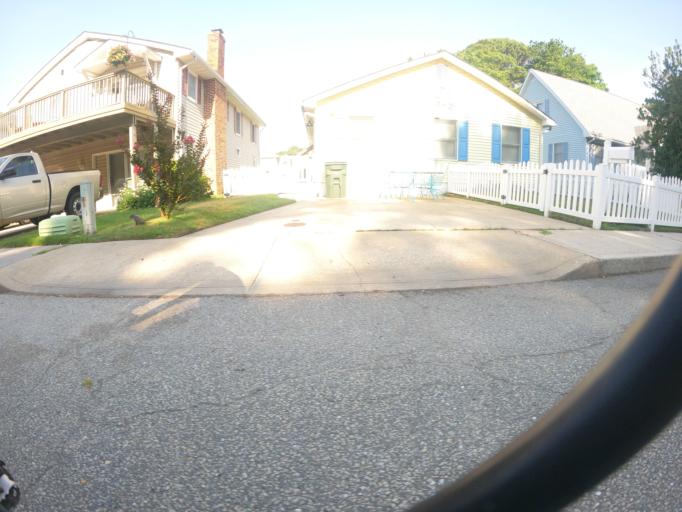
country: US
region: Delaware
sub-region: Sussex County
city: Bethany Beach
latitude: 38.4474
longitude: -75.0610
